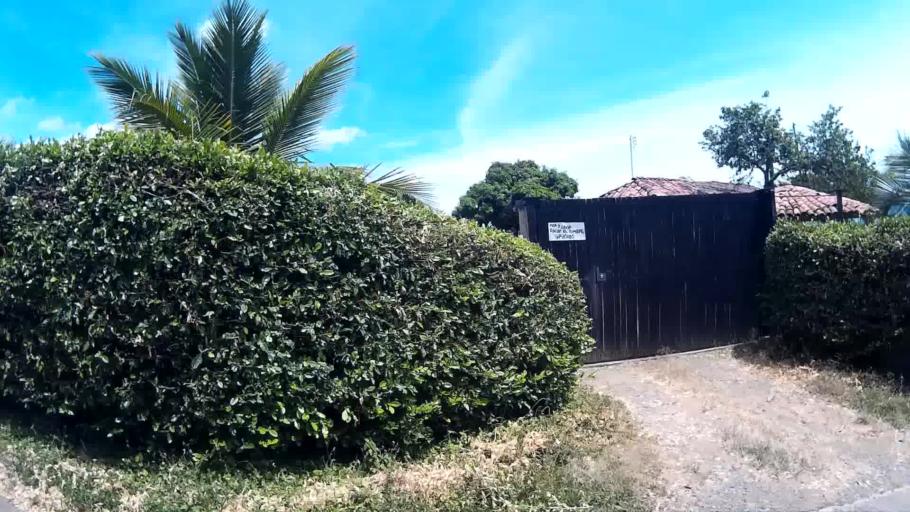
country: CO
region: Caldas
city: Belalcazar
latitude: 4.9449
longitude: -75.8370
